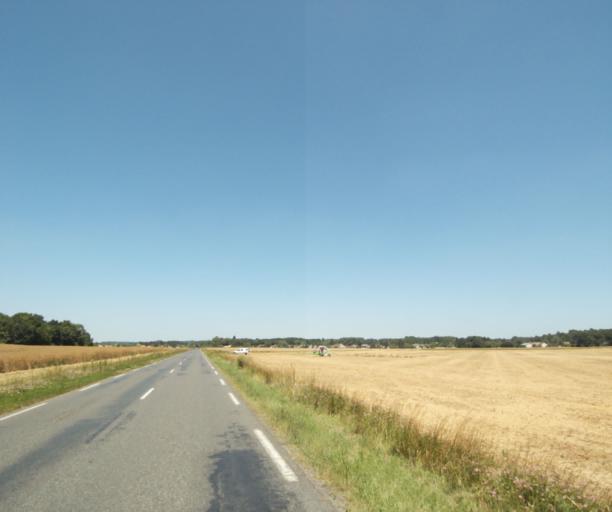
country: FR
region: Ile-de-France
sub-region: Departement de l'Essonne
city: Milly-la-Foret
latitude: 48.3705
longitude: 2.4720
